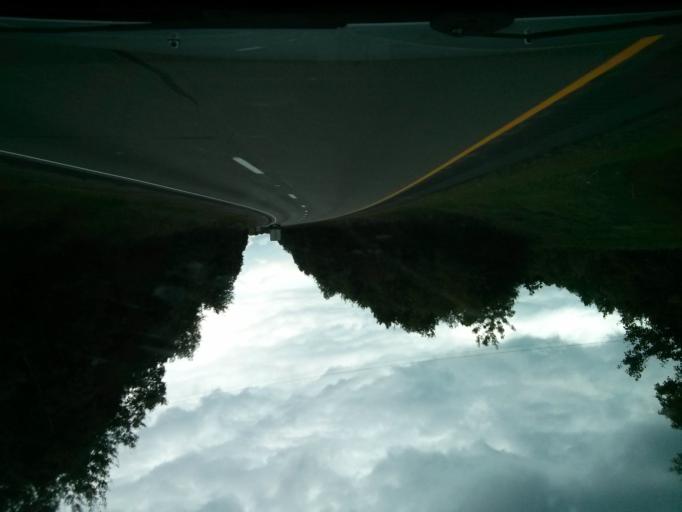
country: US
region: Pennsylvania
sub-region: Clarion County
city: Clarion
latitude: 41.1769
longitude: -79.2518
